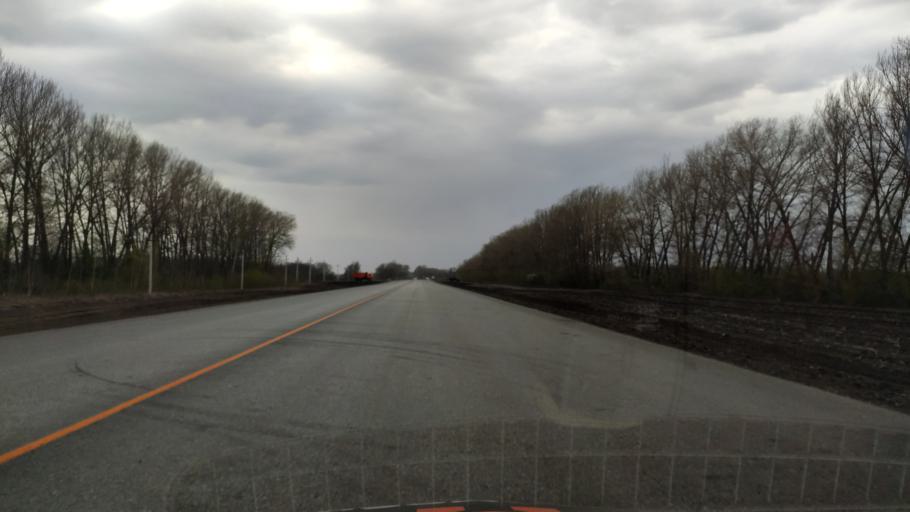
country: RU
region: Kursk
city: Gorshechnoye
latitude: 51.5477
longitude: 38.0789
